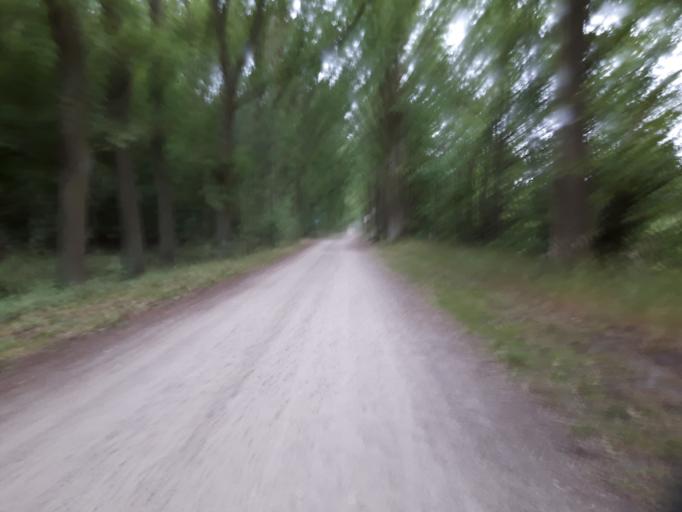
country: DE
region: Lower Saxony
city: Winsen
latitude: 53.3181
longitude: 10.1974
